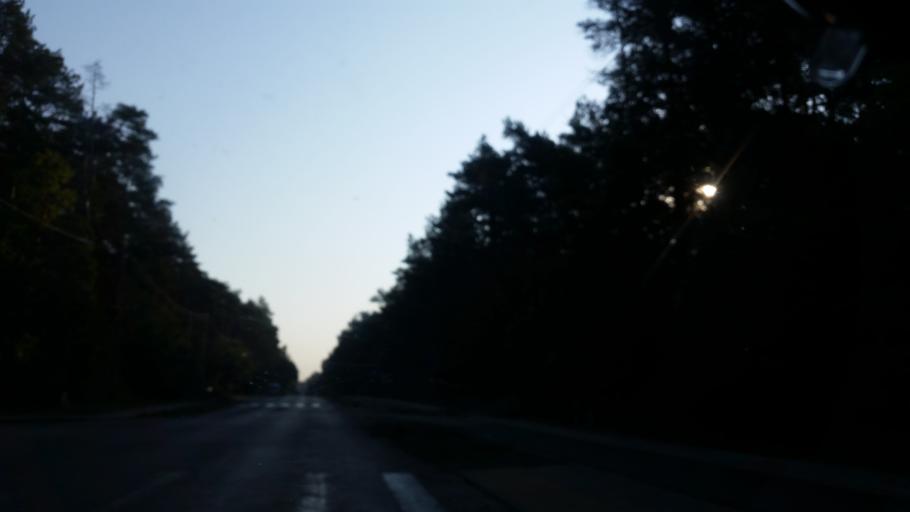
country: PL
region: Masovian Voivodeship
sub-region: Powiat otwocki
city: Jozefow
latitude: 52.1441
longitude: 21.2062
